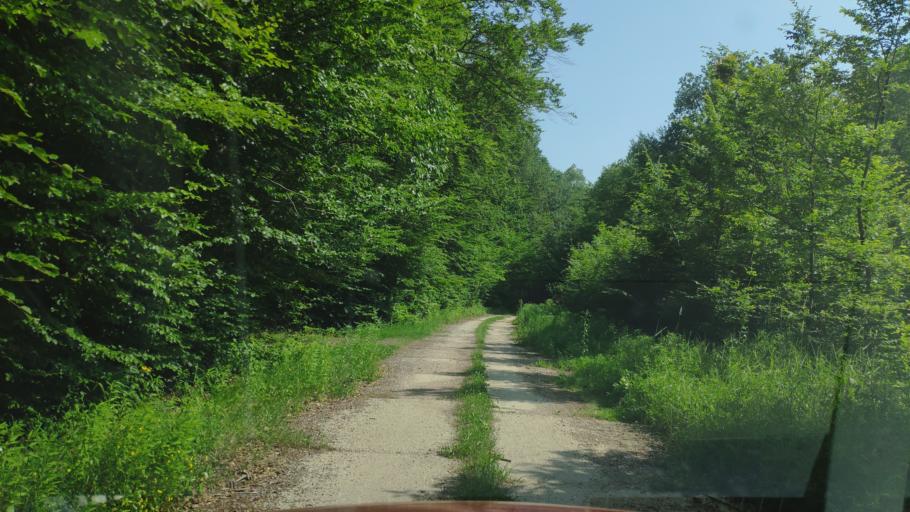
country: SK
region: Presovsky
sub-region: Okres Presov
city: Presov
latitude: 48.9732
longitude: 21.1496
